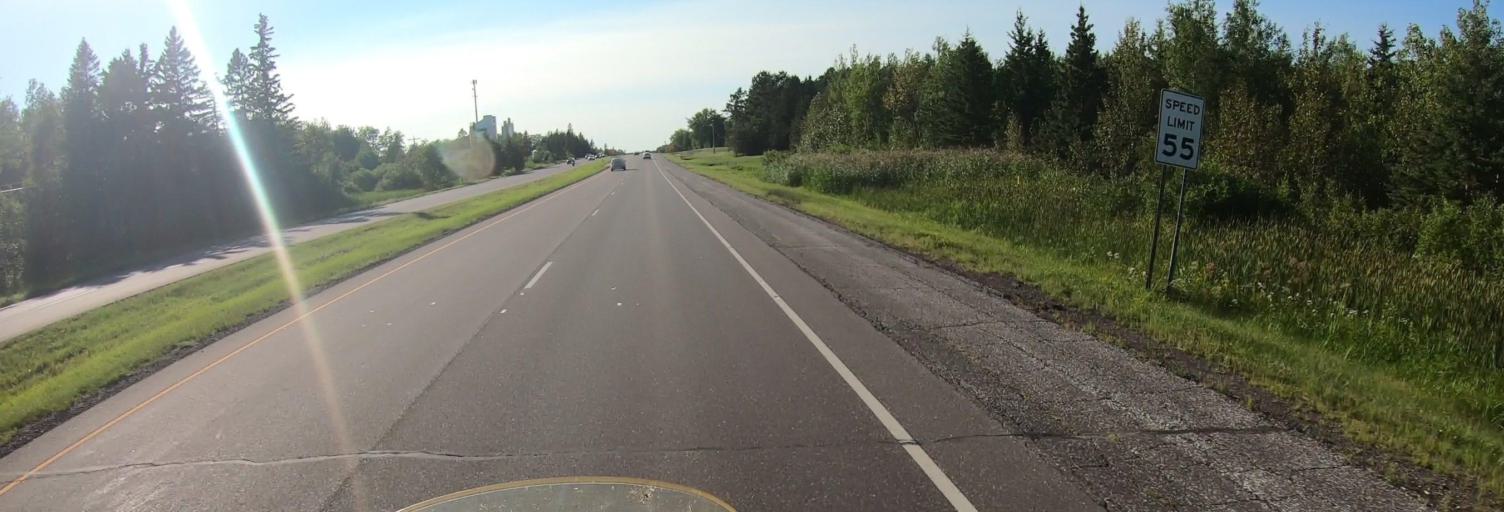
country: US
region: Minnesota
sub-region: Saint Louis County
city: Hermantown
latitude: 46.8455
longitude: -92.2616
